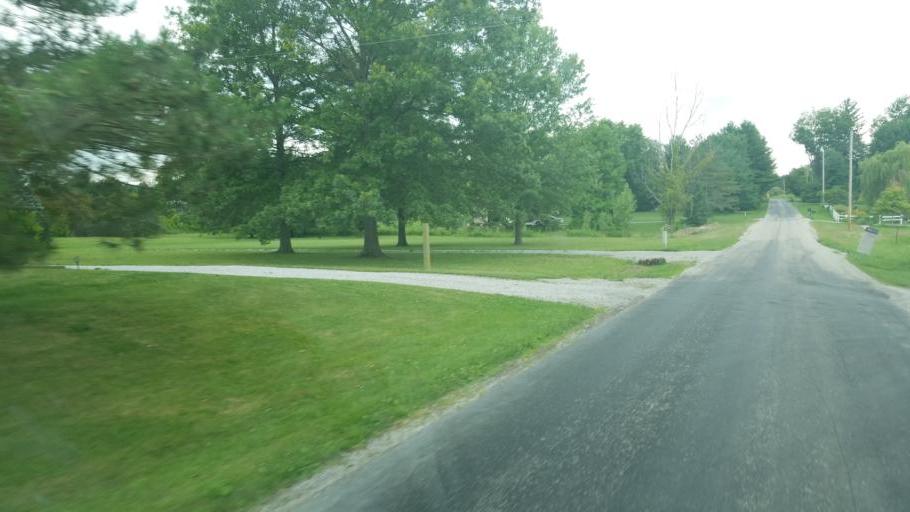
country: US
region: Ohio
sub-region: Delaware County
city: Sunbury
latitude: 40.2788
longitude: -82.8285
